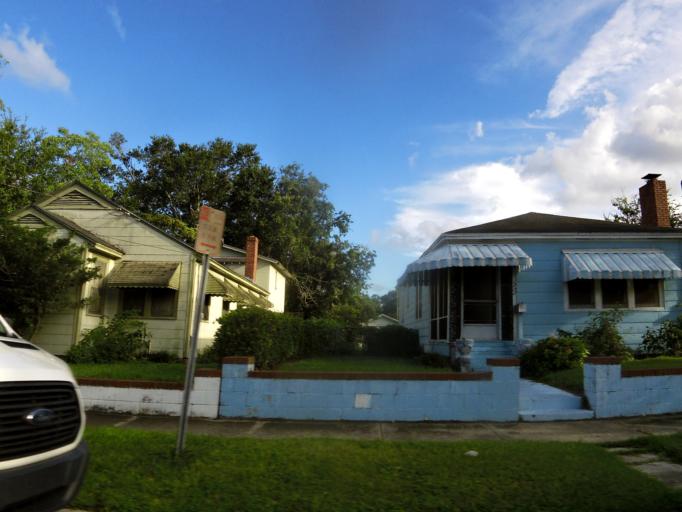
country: US
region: Florida
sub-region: Duval County
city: Jacksonville
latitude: 30.3506
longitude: -81.6742
